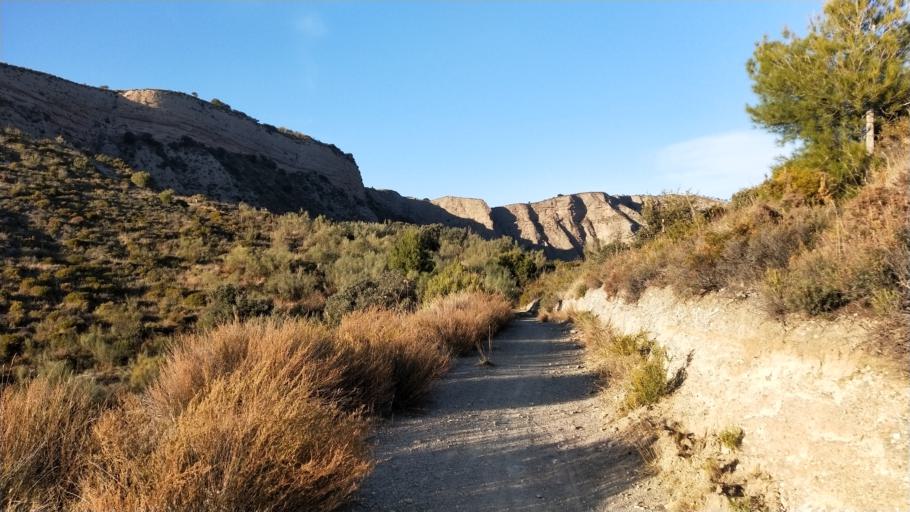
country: ES
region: Andalusia
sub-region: Provincia de Granada
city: Dudar
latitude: 37.1956
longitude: -3.5011
